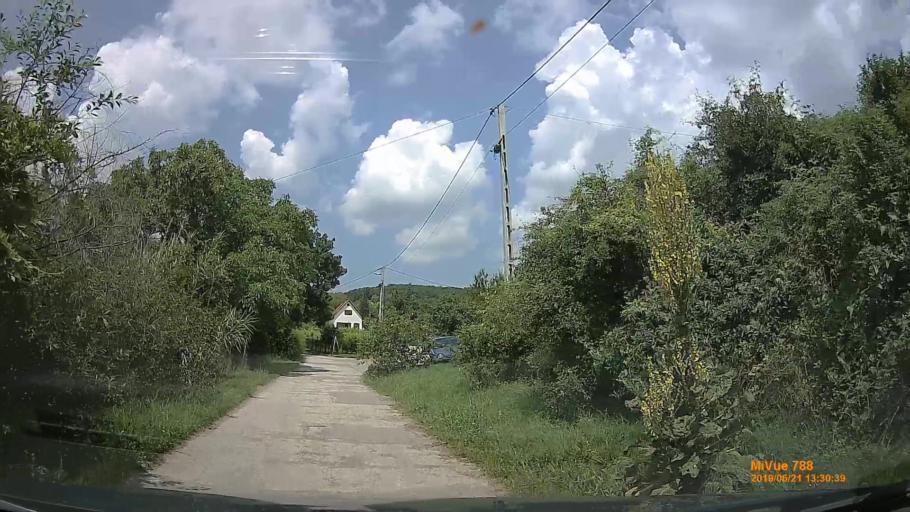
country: HU
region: Baranya
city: Pellerd
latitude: 46.0633
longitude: 18.1371
